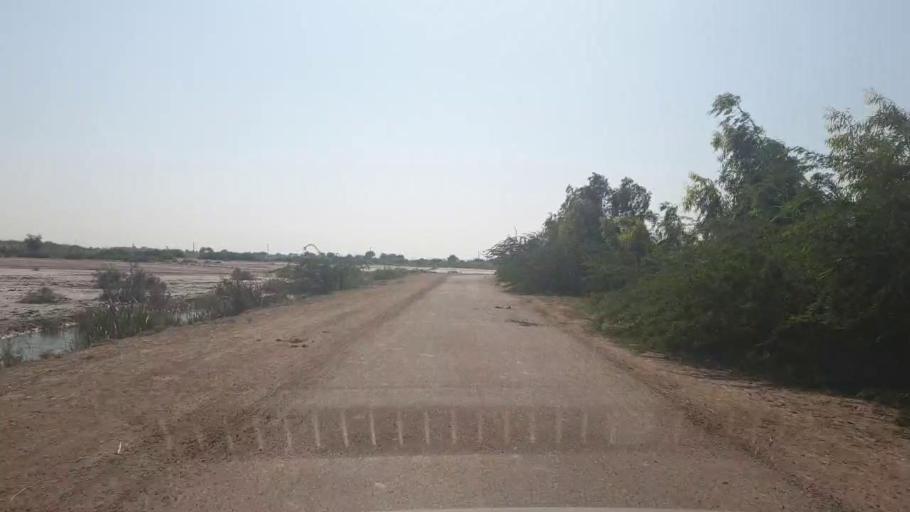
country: PK
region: Sindh
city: Badin
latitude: 24.5552
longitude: 68.8375
